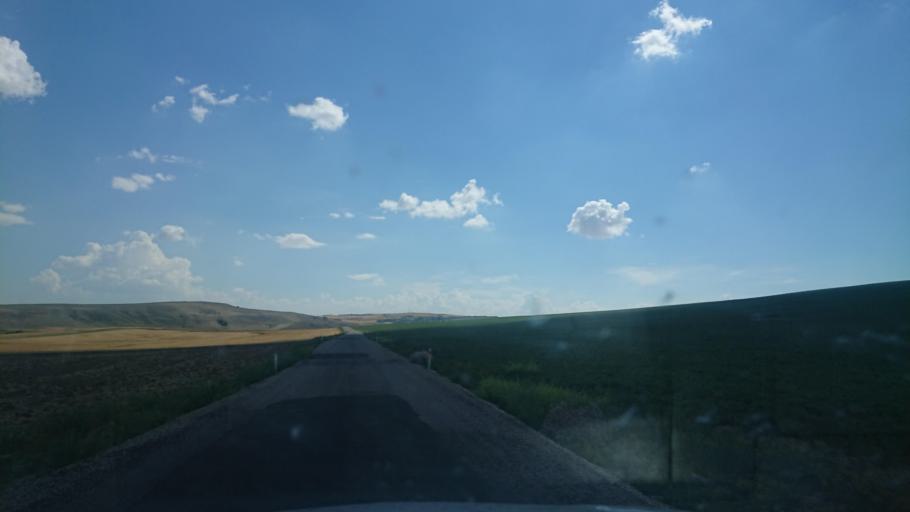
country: TR
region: Aksaray
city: Agacoren
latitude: 38.7913
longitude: 33.8144
